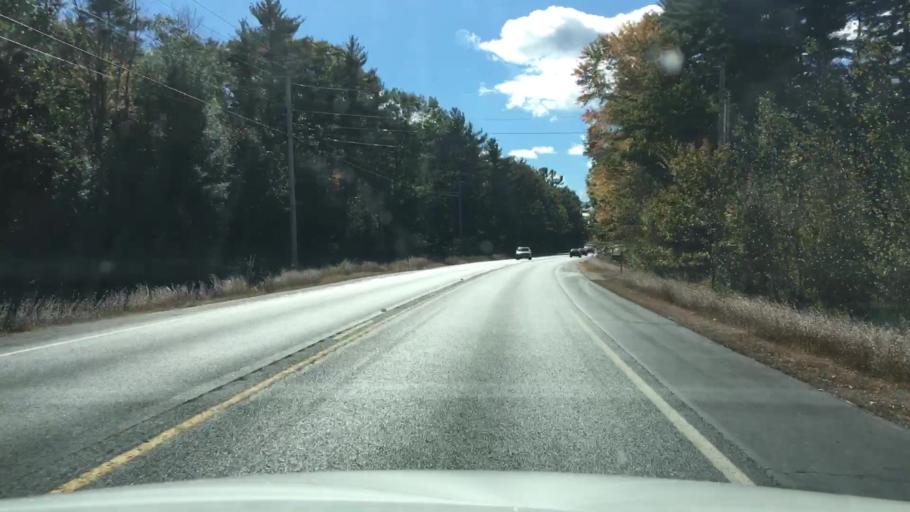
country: US
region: Maine
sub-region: York County
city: South Sanford
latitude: 43.4233
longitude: -70.7339
